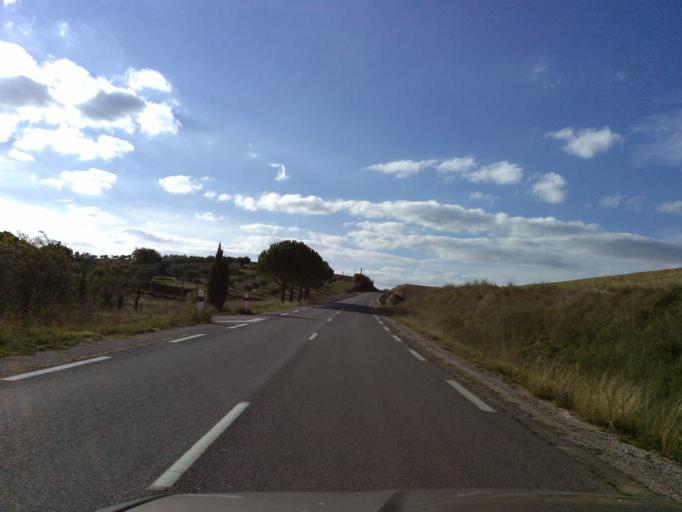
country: FR
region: Provence-Alpes-Cote d'Azur
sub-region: Departement des Alpes-de-Haute-Provence
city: Valensole
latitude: 43.8373
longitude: 5.9682
